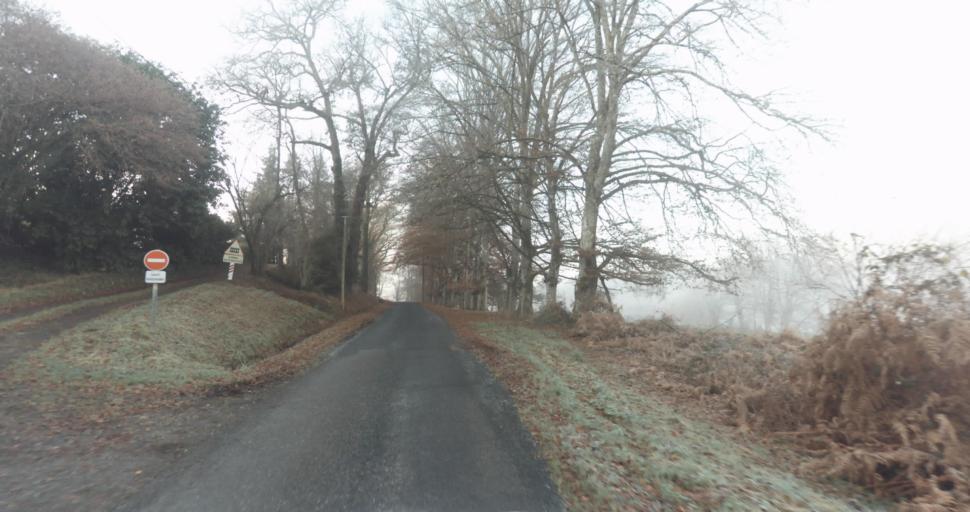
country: FR
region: Limousin
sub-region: Departement de la Haute-Vienne
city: Saint-Priest-sous-Aixe
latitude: 45.8139
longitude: 1.1189
